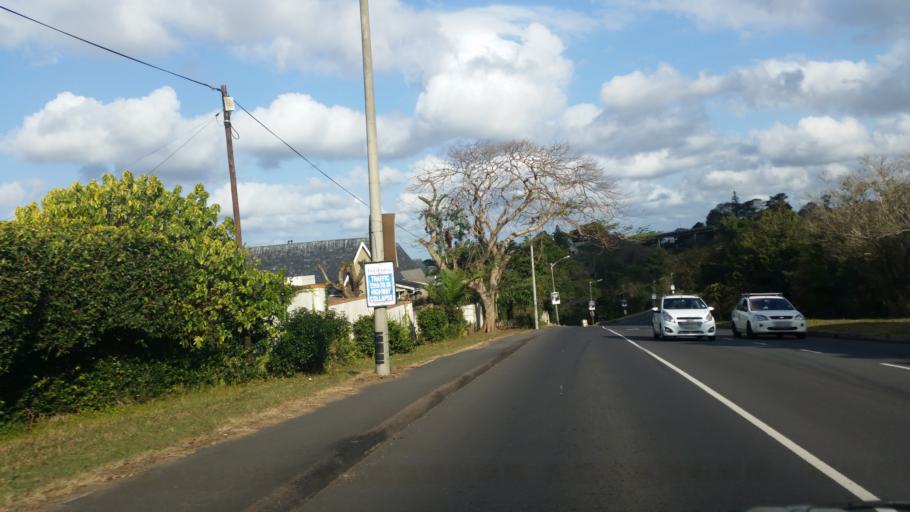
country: ZA
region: KwaZulu-Natal
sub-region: eThekwini Metropolitan Municipality
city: Berea
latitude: -29.8414
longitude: 30.9270
